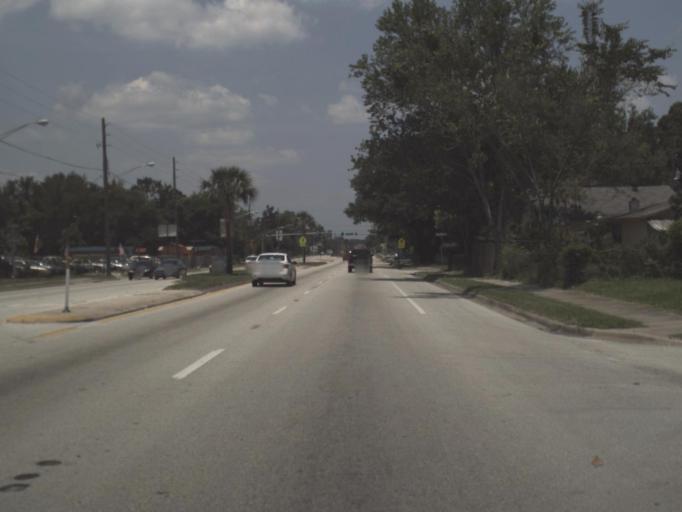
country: US
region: Florida
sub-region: Duval County
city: Jacksonville
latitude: 30.3488
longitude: -81.7310
